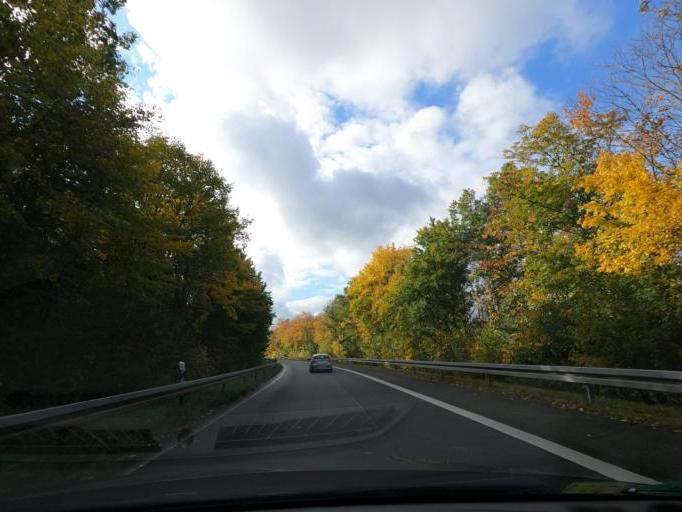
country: DE
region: Lower Saxony
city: Leiferde
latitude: 52.2026
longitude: 10.5288
